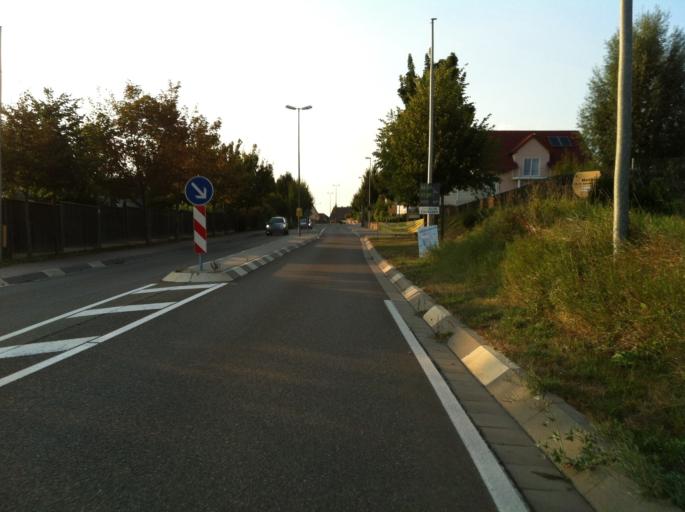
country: DE
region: Rheinland-Pfalz
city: Schwabenheim
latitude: 49.9258
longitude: 8.1013
